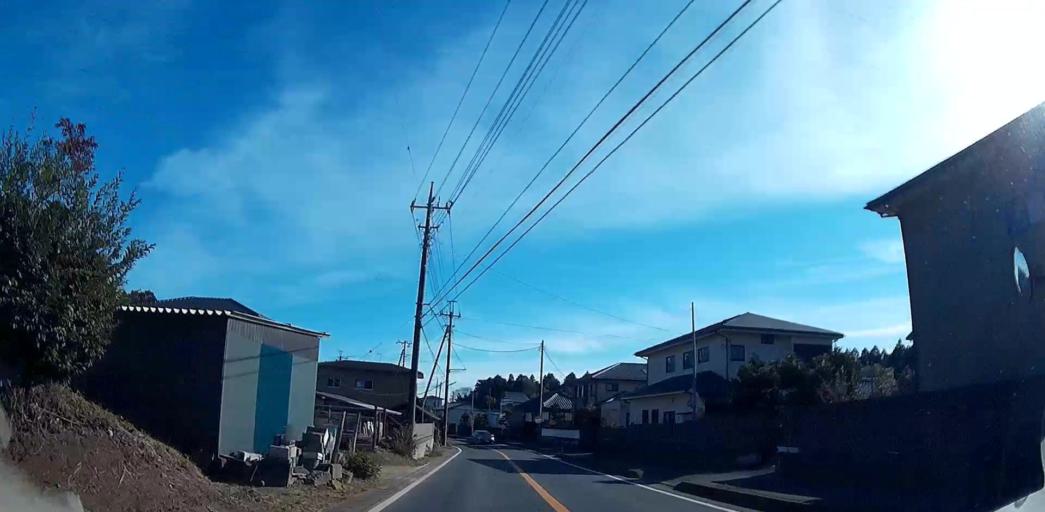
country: JP
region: Chiba
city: Yokaichiba
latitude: 35.7380
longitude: 140.4851
